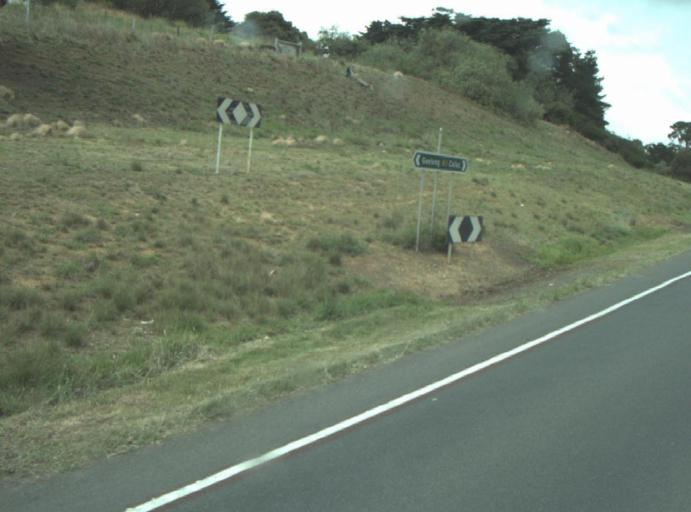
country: AU
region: Victoria
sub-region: Greater Geelong
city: Wandana Heights
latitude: -38.2075
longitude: 144.2734
